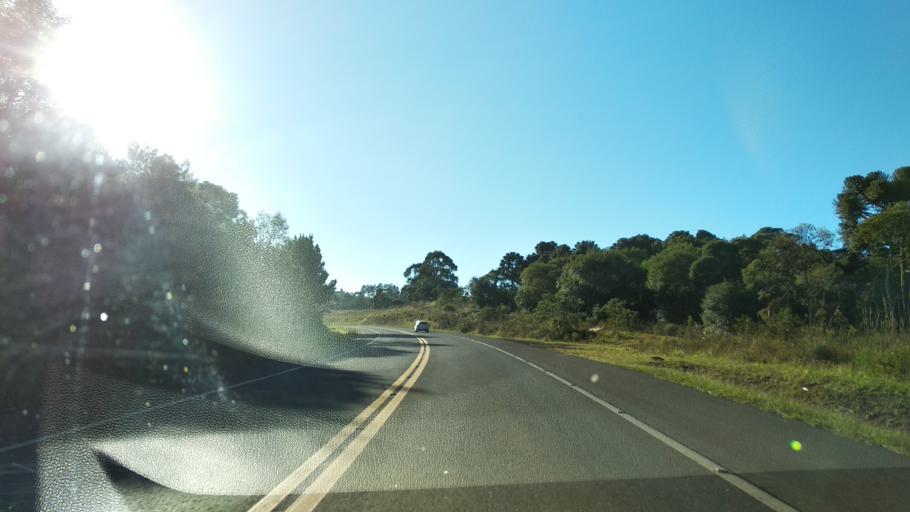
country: BR
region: Santa Catarina
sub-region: Lages
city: Lages
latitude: -27.7912
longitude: -50.4161
